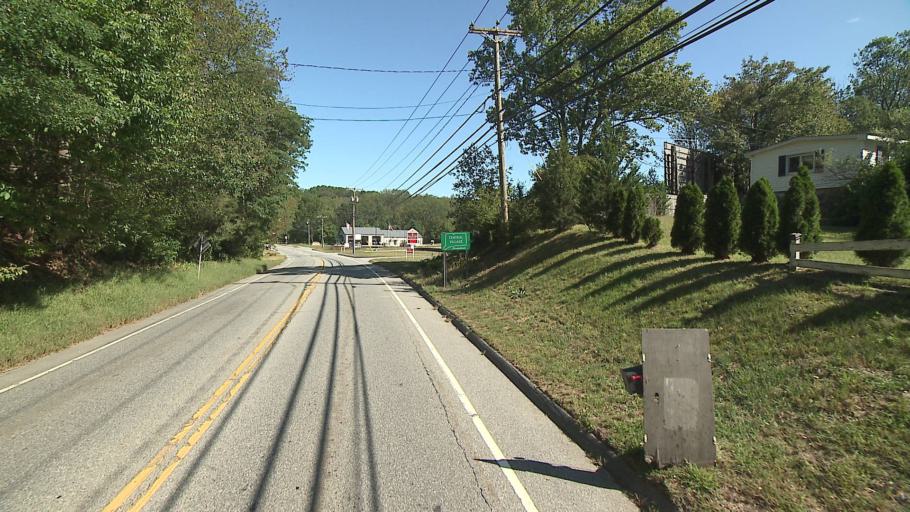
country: US
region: Connecticut
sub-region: Windham County
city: Moosup
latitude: 41.7156
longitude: -71.9032
